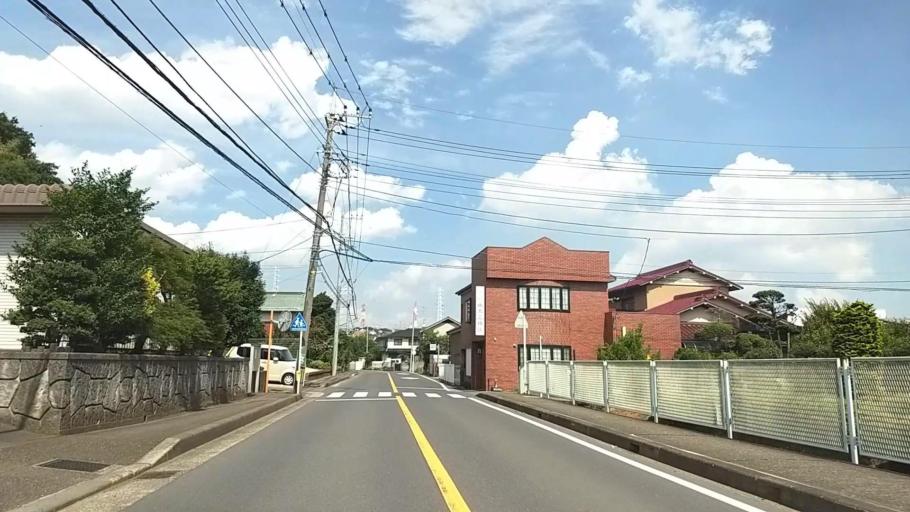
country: JP
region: Kanagawa
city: Yokohama
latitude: 35.5279
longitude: 139.5908
